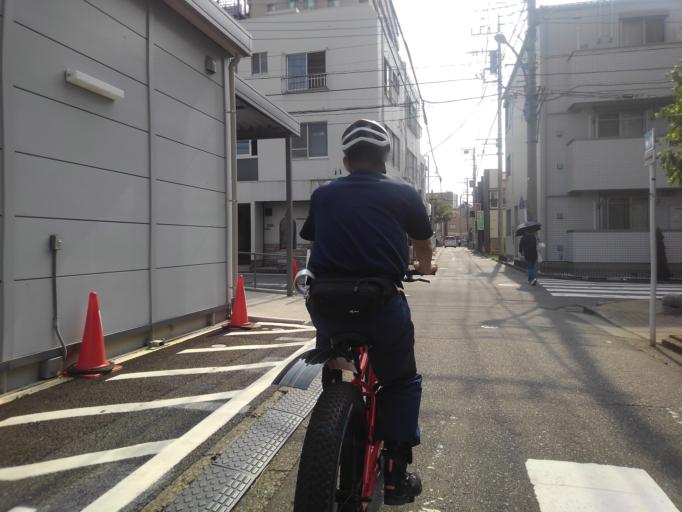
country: JP
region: Kanagawa
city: Minami-rinkan
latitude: 35.4693
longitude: 139.4591
